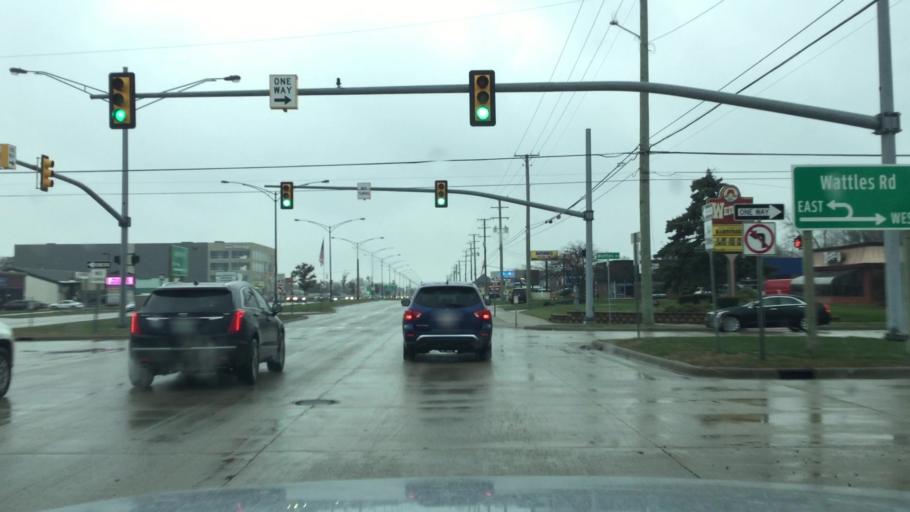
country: US
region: Michigan
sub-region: Oakland County
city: Troy
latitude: 42.5779
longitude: -83.1286
